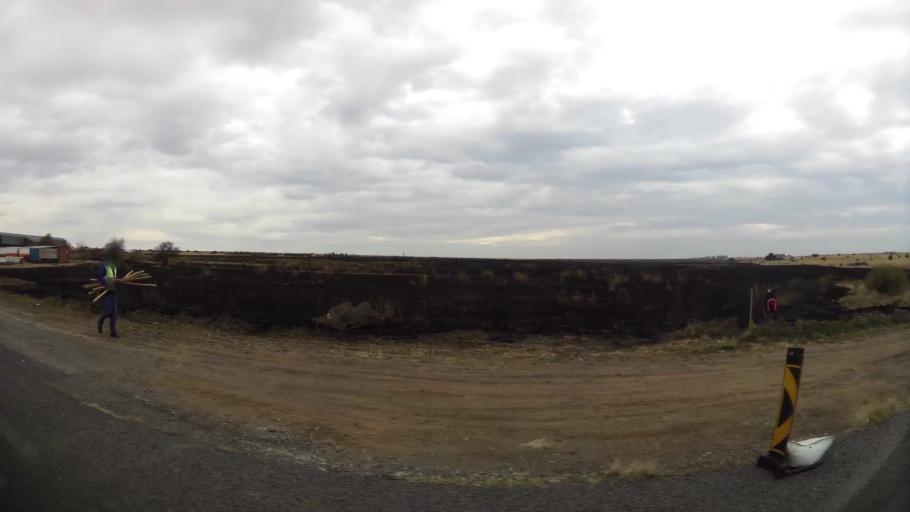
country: ZA
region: Orange Free State
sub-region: Fezile Dabi District Municipality
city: Kroonstad
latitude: -27.6232
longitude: 27.2473
